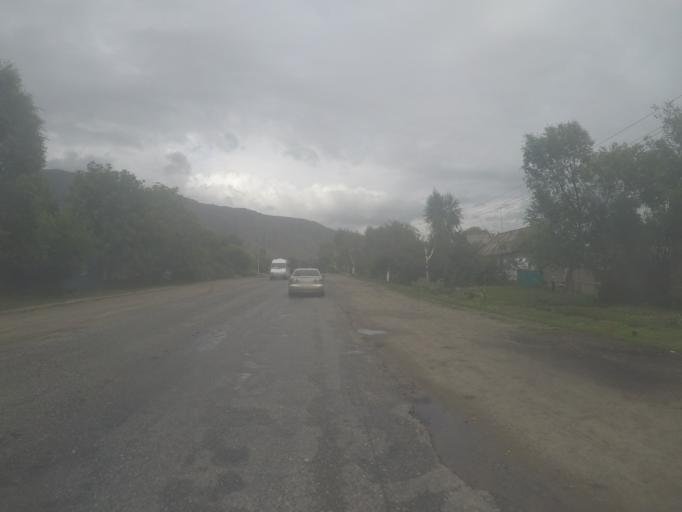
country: KG
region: Ysyk-Koel
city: Tyup
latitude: 42.7402
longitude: 78.0109
